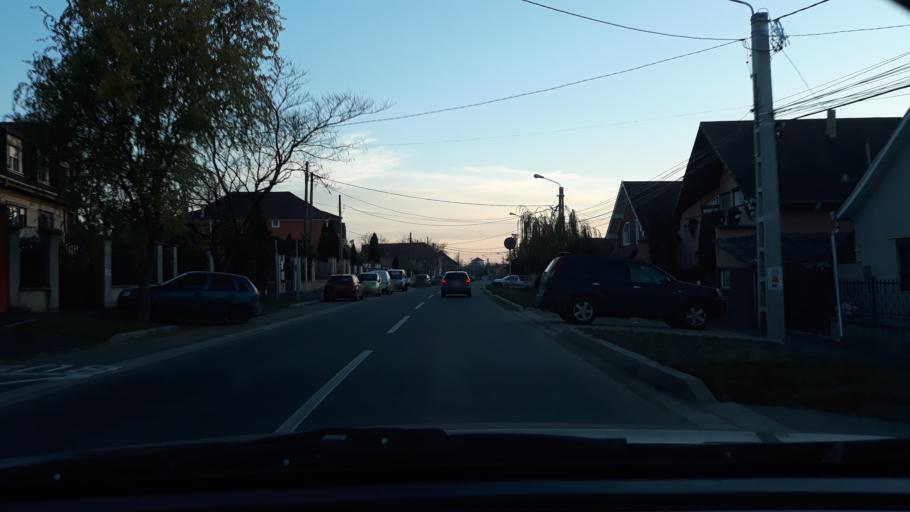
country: RO
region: Bihor
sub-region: Comuna Biharea
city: Oradea
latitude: 47.0884
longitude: 21.9267
